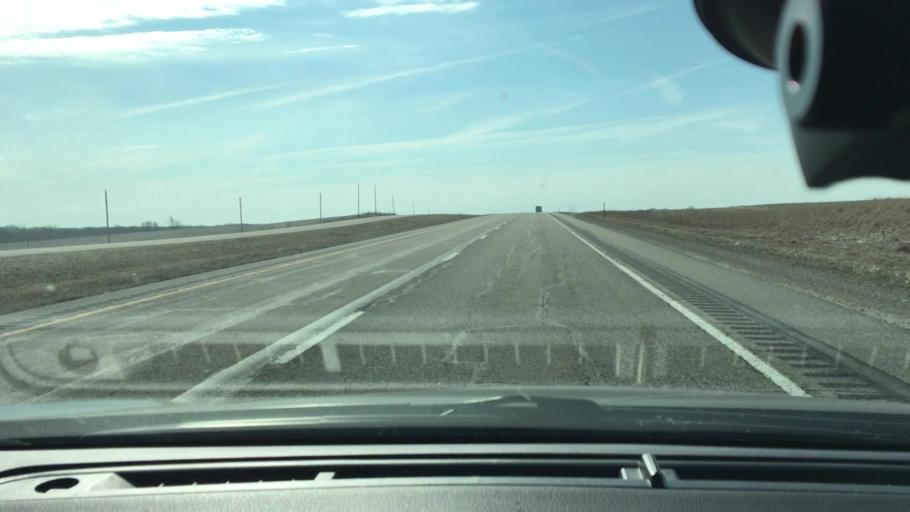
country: US
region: Iowa
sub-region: Chickasaw County
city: Nashua
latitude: 42.9896
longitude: -92.5915
